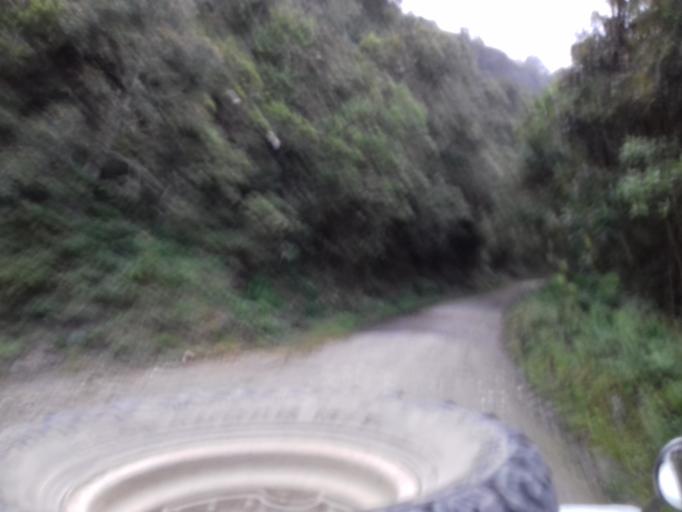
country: CO
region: Quindio
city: Salento
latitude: 4.5586
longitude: -75.5177
